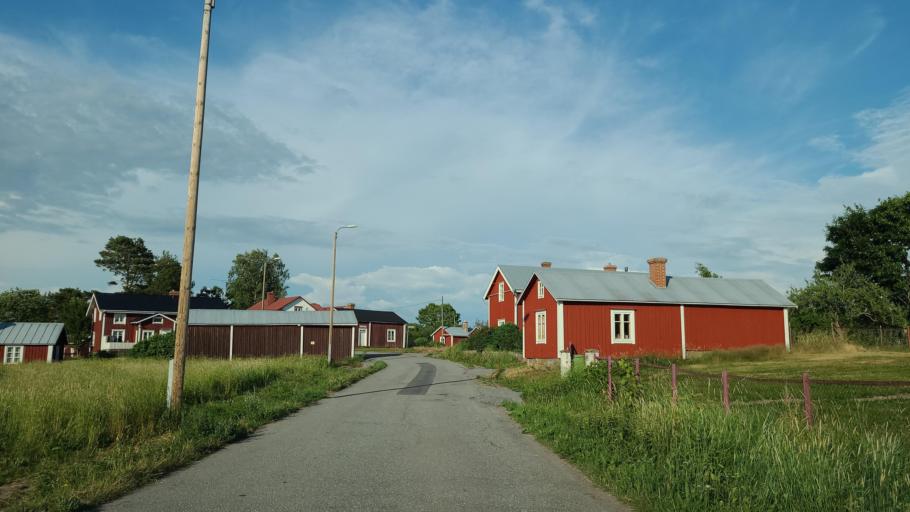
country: FI
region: Ostrobothnia
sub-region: Vaasa
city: Replot
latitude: 63.3459
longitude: 21.3352
